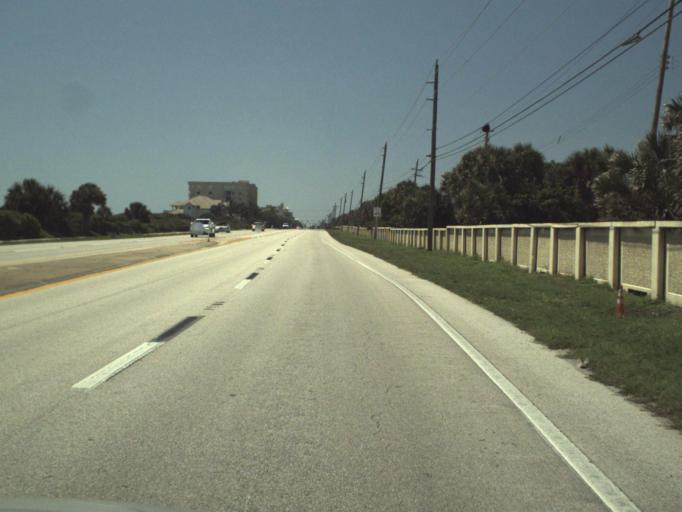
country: US
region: Florida
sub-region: Brevard County
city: South Patrick Shores
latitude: 28.1936
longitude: -80.5948
